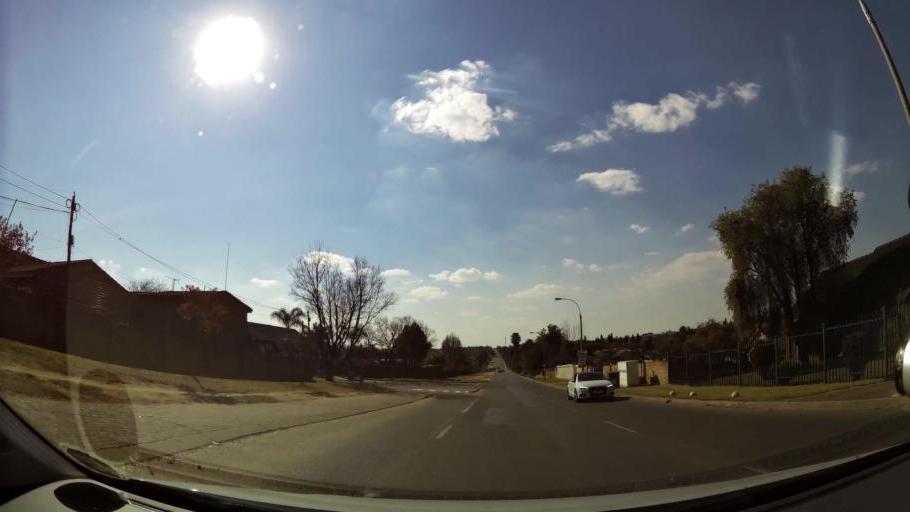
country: ZA
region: Gauteng
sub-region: Ekurhuleni Metropolitan Municipality
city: Tembisa
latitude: -26.0695
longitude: 28.2486
